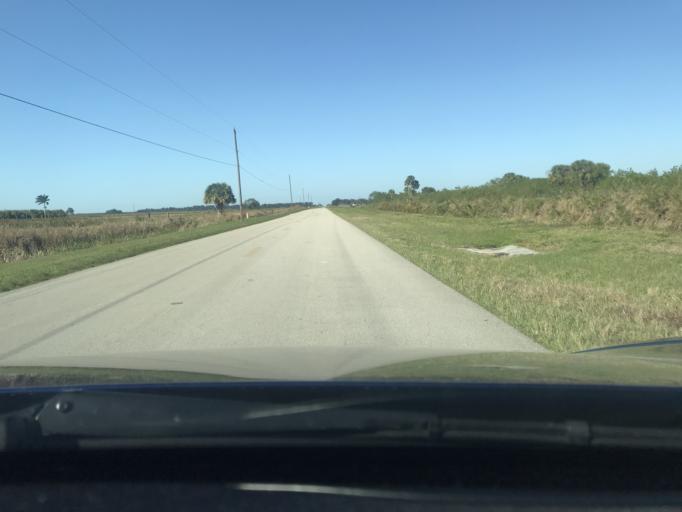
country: US
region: Florida
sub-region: Saint Lucie County
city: Fort Pierce South
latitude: 27.4066
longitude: -80.4975
